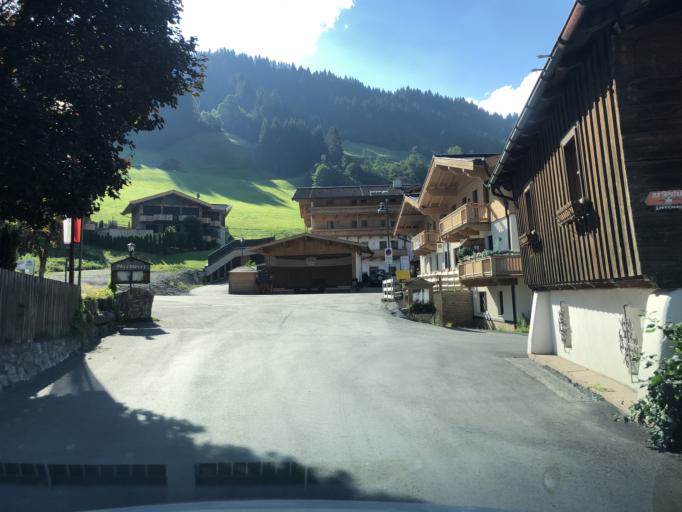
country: AT
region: Tyrol
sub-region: Politischer Bezirk Kitzbuhel
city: Kirchberg in Tirol
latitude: 47.3823
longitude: 12.3101
